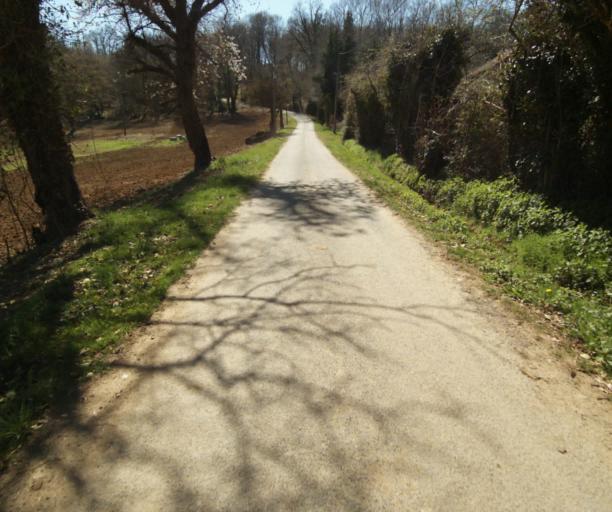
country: FR
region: Limousin
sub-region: Departement de la Correze
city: Uzerche
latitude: 45.3927
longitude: 1.6076
